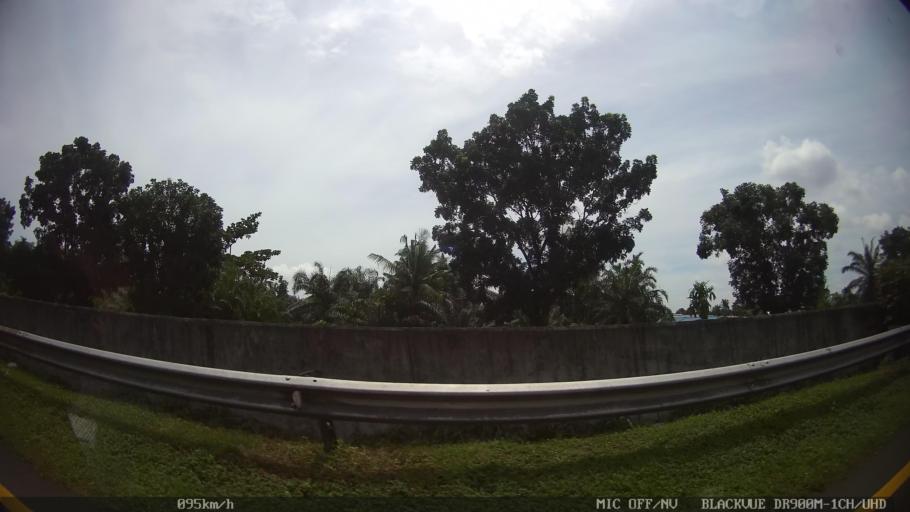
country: ID
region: North Sumatra
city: Labuhan Deli
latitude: 3.7093
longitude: 98.6819
